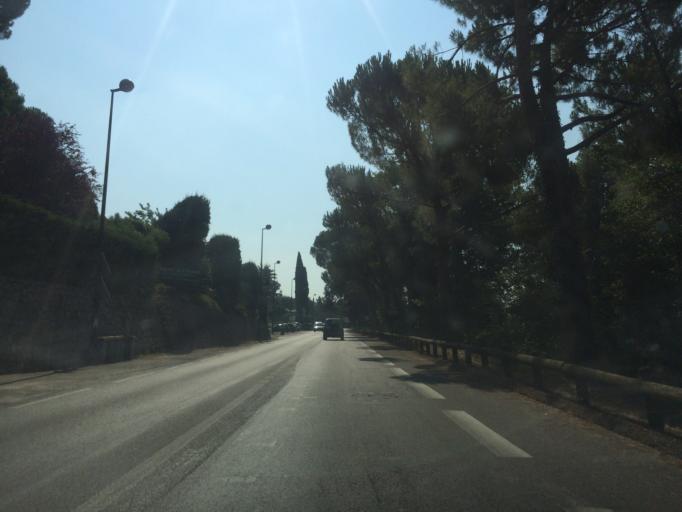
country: FR
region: Provence-Alpes-Cote d'Azur
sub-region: Departement des Alpes-Maritimes
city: Saint-Paul-de-Vence
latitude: 43.6998
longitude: 7.1100
